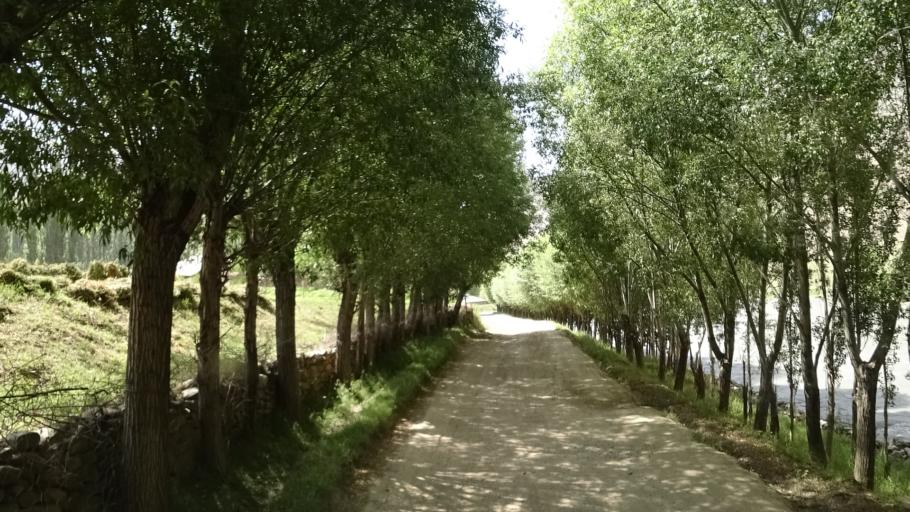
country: TJ
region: Gorno-Badakhshan
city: Khorugh
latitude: 37.1805
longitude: 71.4509
